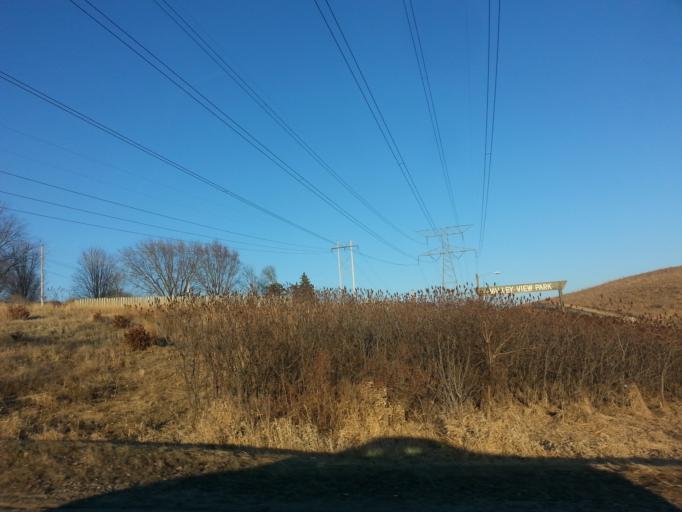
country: US
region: Minnesota
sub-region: Washington County
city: Oak Park Heights
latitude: 45.0281
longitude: -92.8073
